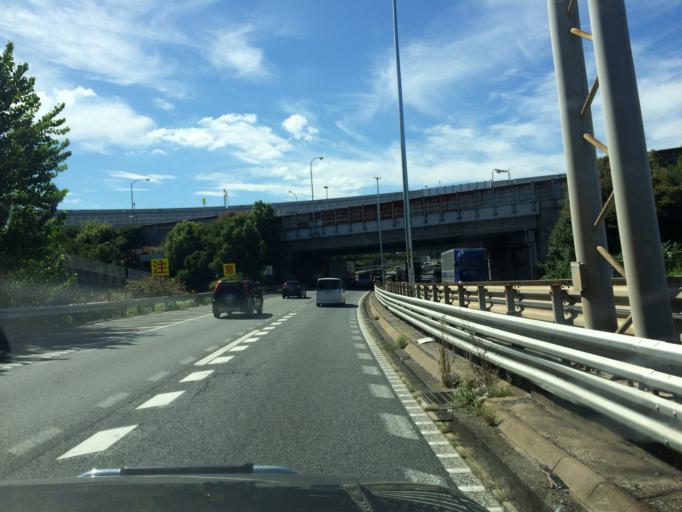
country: JP
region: Osaka
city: Yao
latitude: 34.5910
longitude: 135.5759
